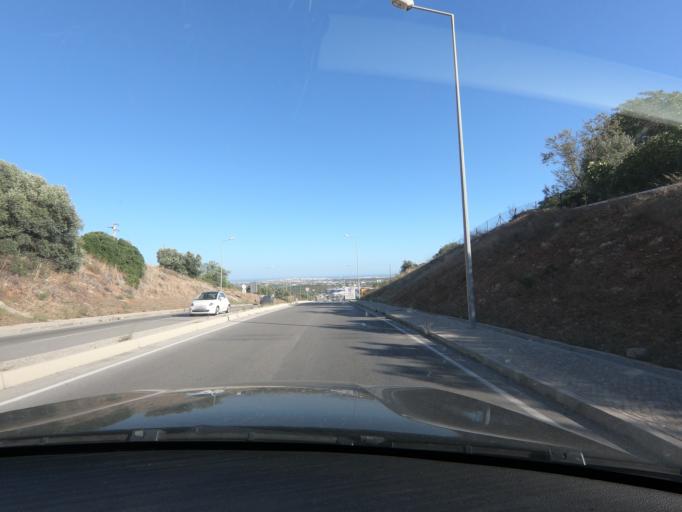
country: PT
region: Faro
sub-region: Faro
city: Santa Barbara de Nexe
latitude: 37.1056
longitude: -8.0009
